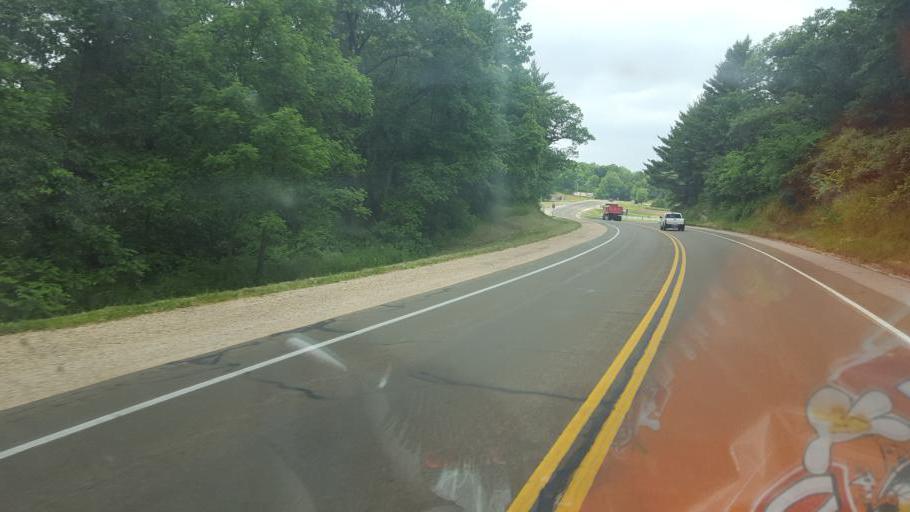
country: US
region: Wisconsin
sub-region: Sauk County
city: Reedsburg
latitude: 43.5819
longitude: -90.1199
